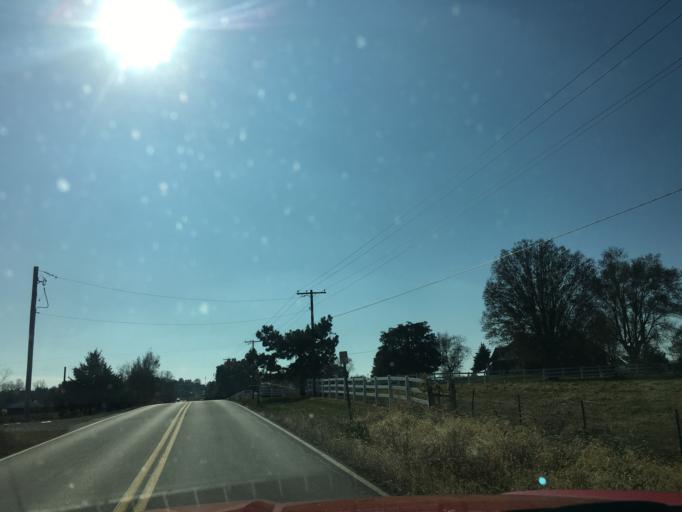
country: US
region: Missouri
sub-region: Cole County
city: Wardsville
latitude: 38.5043
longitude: -92.1758
